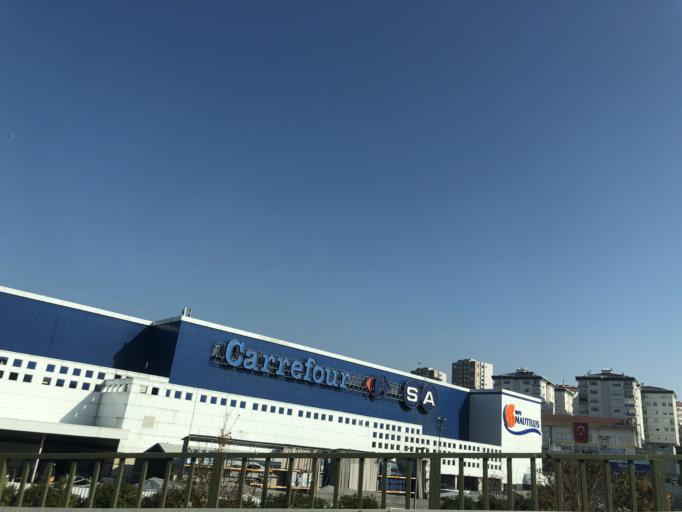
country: TR
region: Istanbul
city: UEskuedar
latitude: 40.9985
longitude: 29.0304
